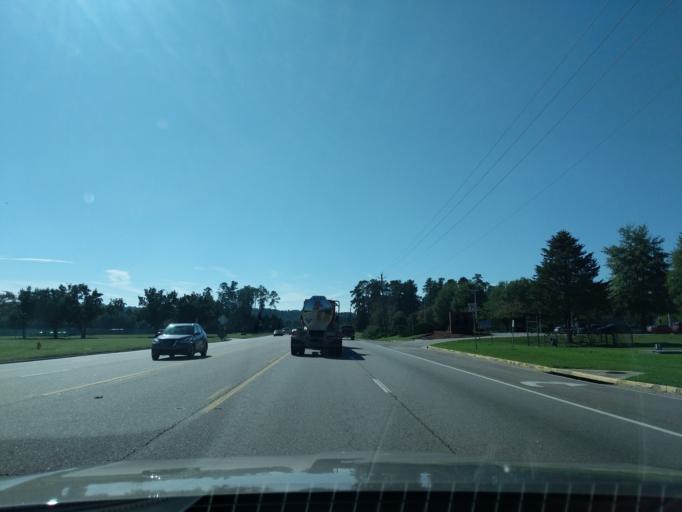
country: US
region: Georgia
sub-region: Richmond County
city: Augusta
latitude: 33.3906
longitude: -82.0050
